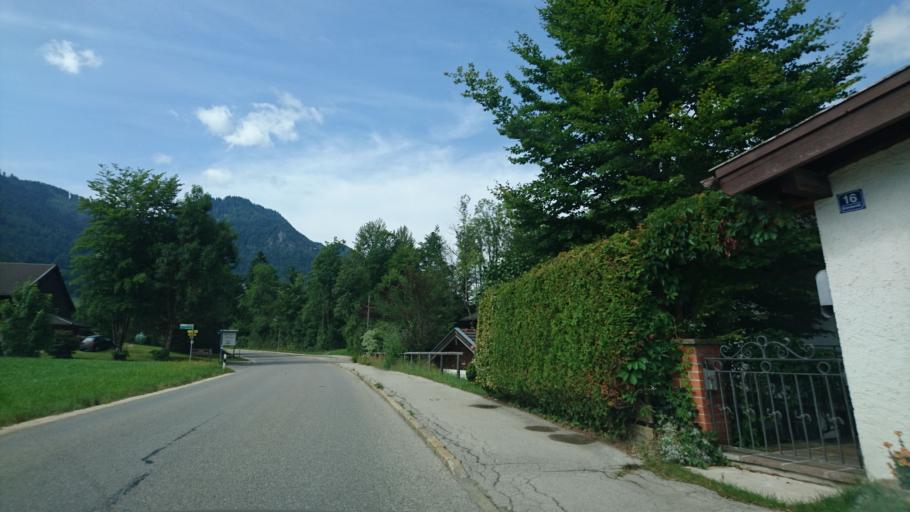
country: DE
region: Bavaria
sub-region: Upper Bavaria
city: Ruhpolding
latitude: 47.7549
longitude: 12.6441
